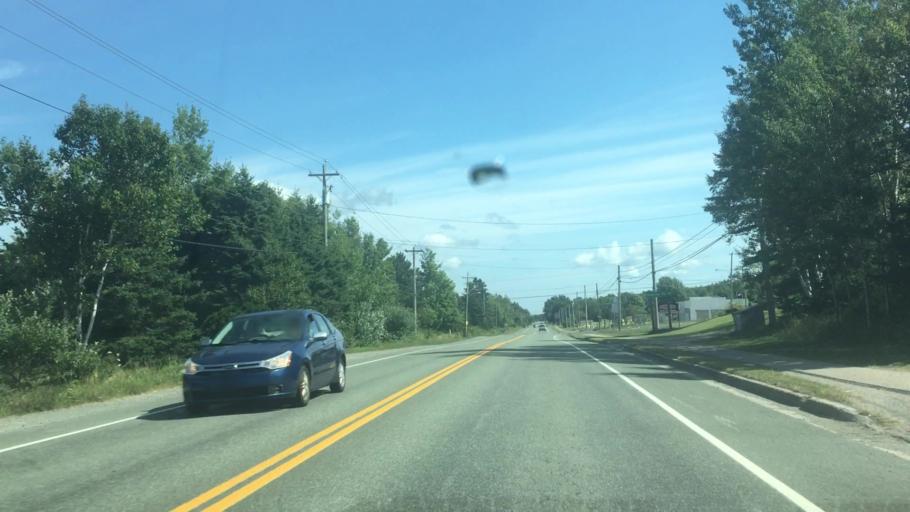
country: CA
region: Nova Scotia
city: Sydney
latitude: 46.0596
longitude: -60.3051
